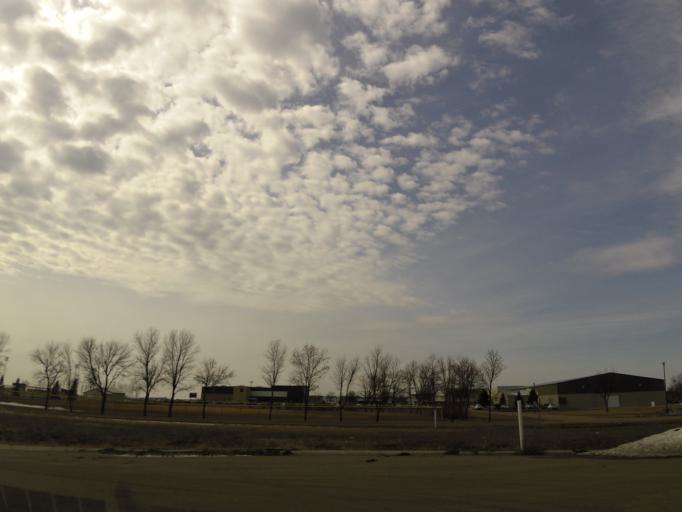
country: US
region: North Dakota
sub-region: Walsh County
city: Grafton
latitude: 48.4068
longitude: -97.4196
